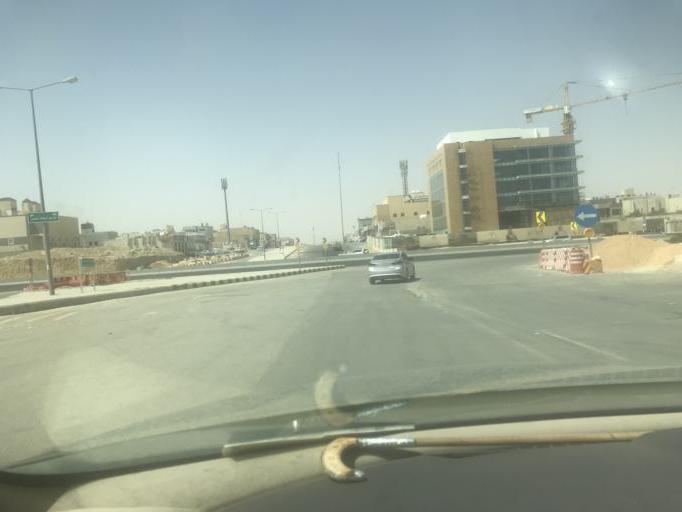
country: SA
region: Ar Riyad
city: Riyadh
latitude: 24.8184
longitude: 46.5966
